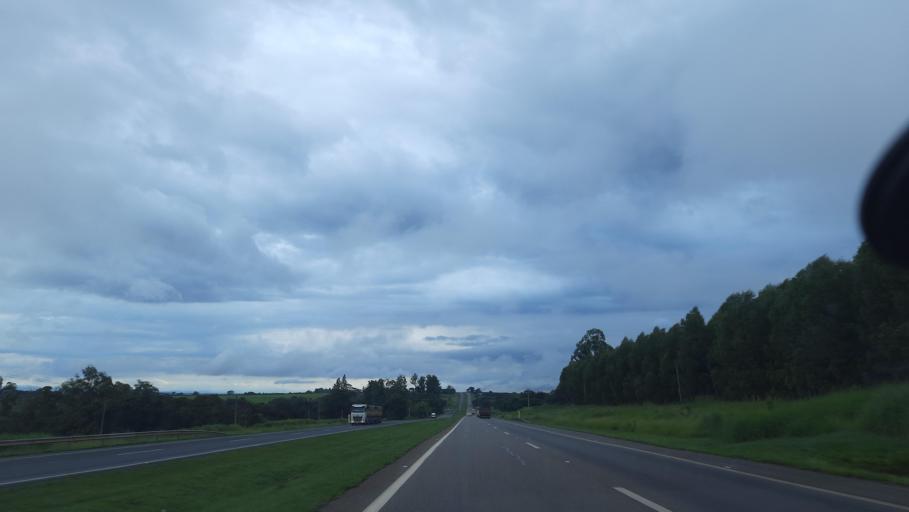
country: BR
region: Sao Paulo
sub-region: Moji-Guacu
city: Mogi-Gaucu
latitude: -22.2352
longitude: -46.9785
